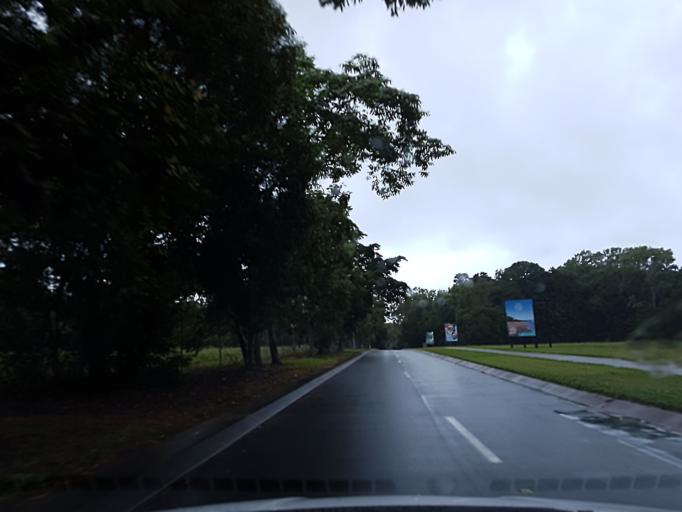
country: AU
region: Queensland
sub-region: Cairns
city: Palm Cove
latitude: -16.7527
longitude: 145.6677
